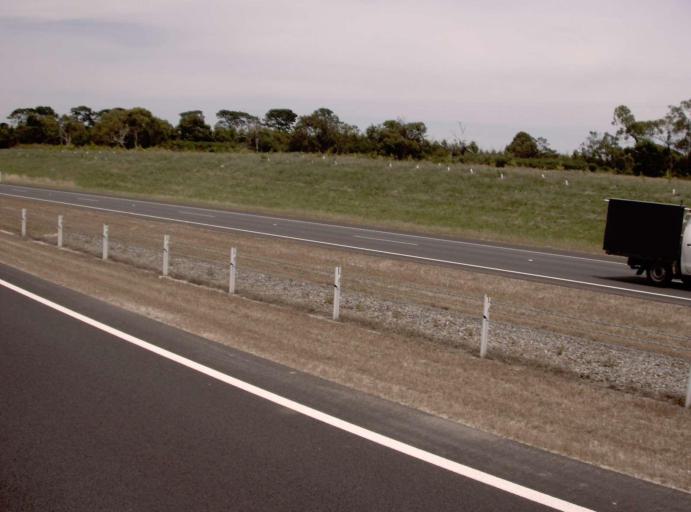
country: AU
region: Victoria
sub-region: Mornington Peninsula
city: Moorooduc
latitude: -38.2130
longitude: 145.1302
